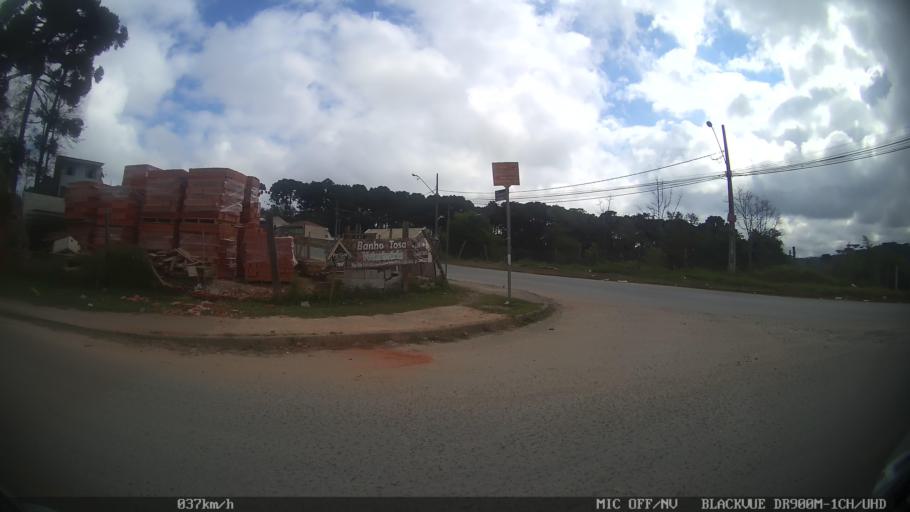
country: BR
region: Parana
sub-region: Colombo
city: Colombo
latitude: -25.3431
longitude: -49.2403
